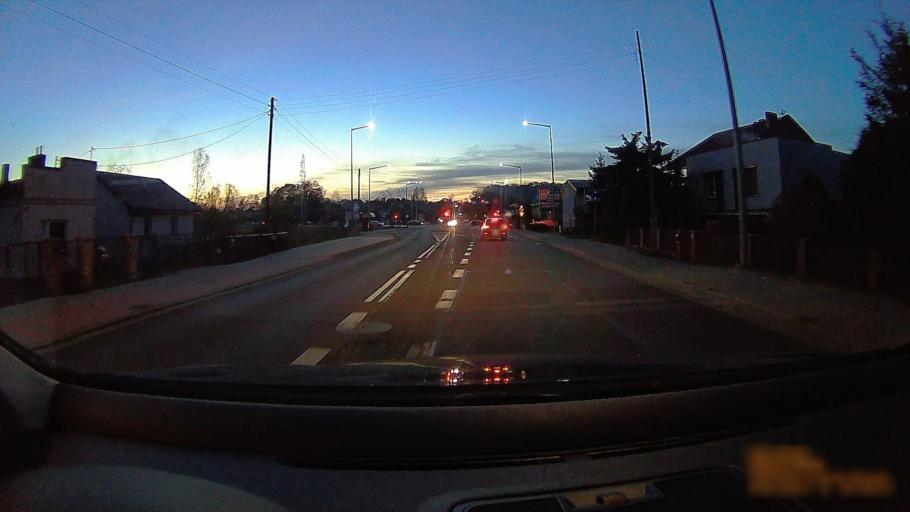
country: PL
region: Greater Poland Voivodeship
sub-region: Powiat koninski
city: Stare Miasto
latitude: 52.2029
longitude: 18.2283
